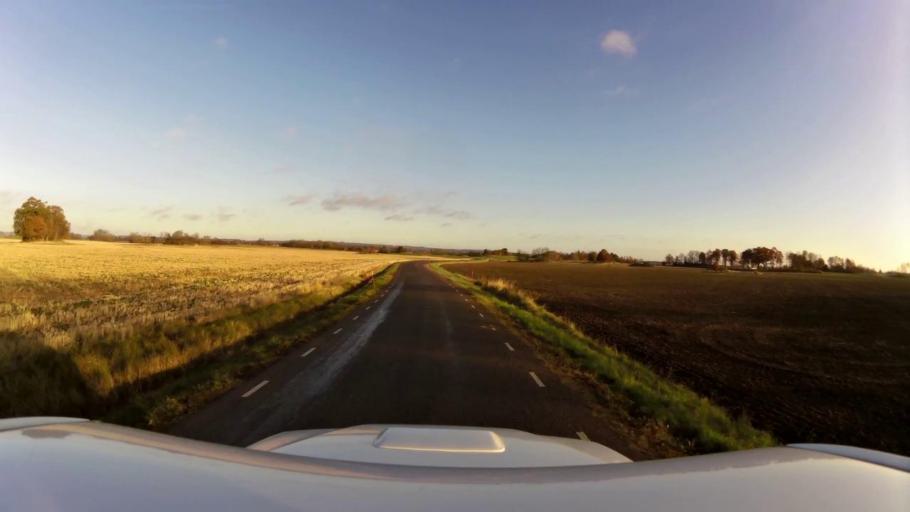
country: SE
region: OEstergoetland
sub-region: Linkopings Kommun
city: Linghem
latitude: 58.4787
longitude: 15.7287
